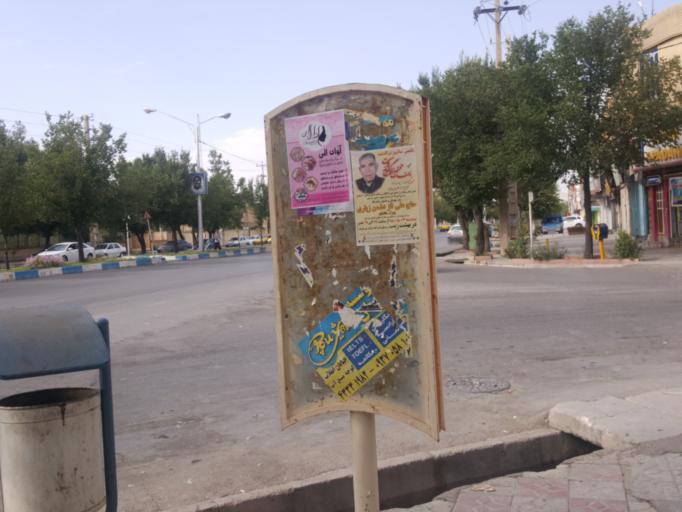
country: IR
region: Fars
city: Marvdasht
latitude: 29.8851
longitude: 52.8126
